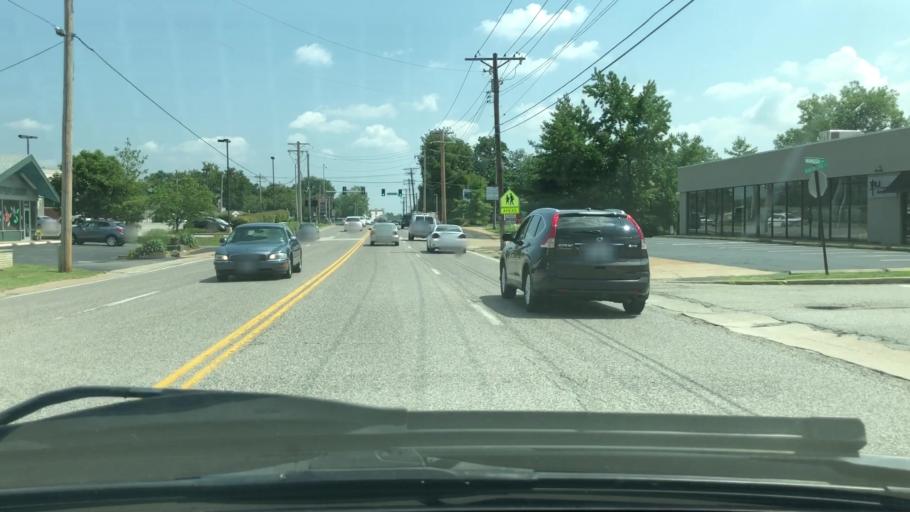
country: US
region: Missouri
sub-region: Saint Louis County
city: Rock Hill
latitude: 38.6063
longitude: -90.3744
